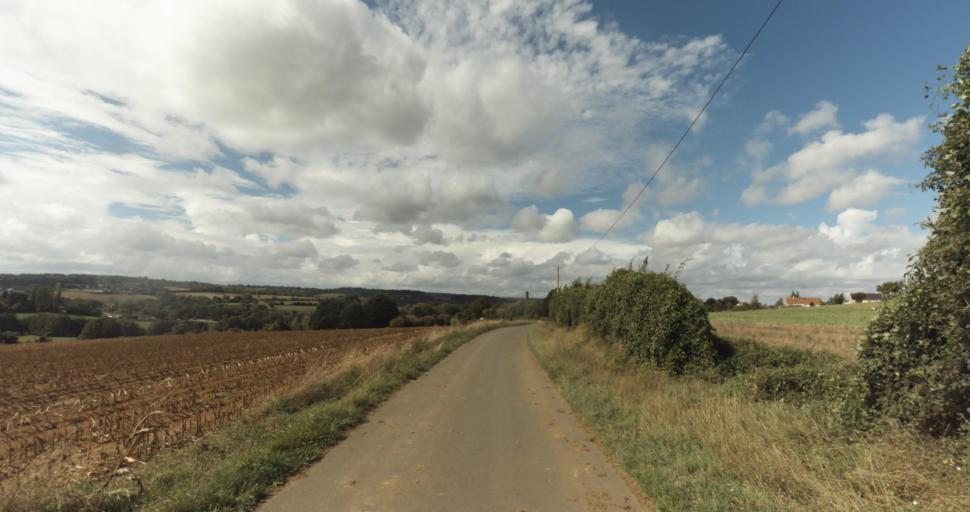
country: FR
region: Lower Normandy
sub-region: Departement de l'Orne
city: Gace
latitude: 48.7824
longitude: 0.3024
